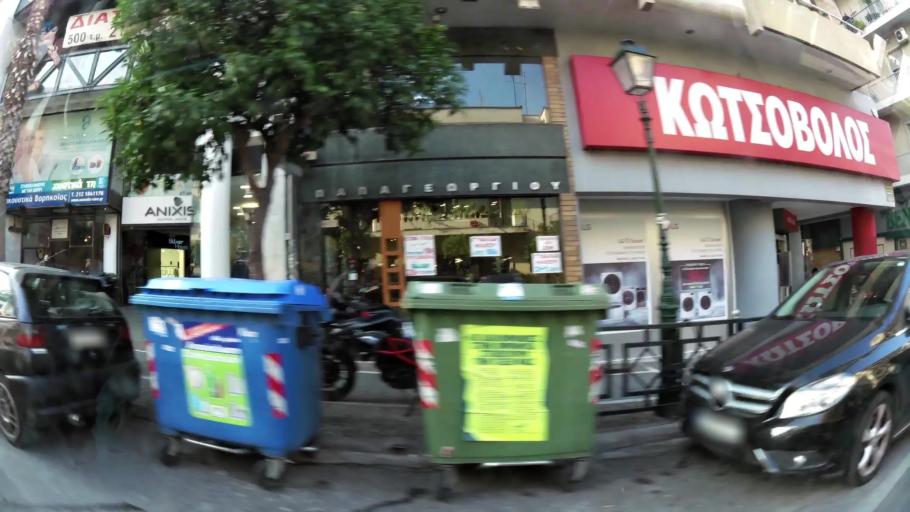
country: GR
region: Attica
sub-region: Nomarchia Athinas
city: Kaisariani
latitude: 37.9791
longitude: 23.7654
